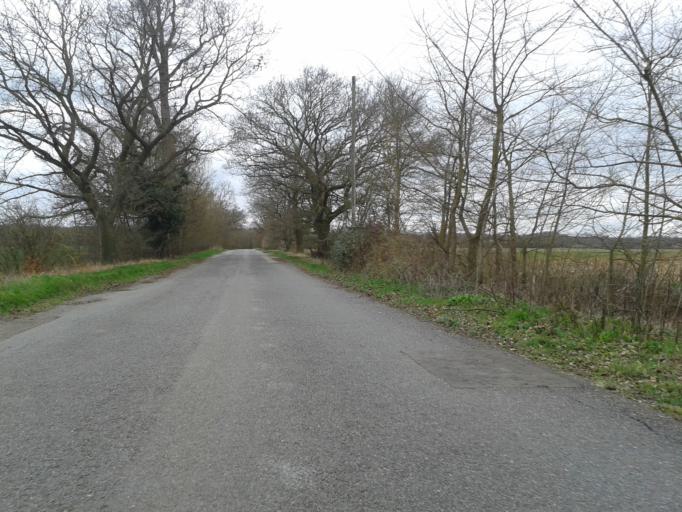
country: GB
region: England
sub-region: Cambridgeshire
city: Girton
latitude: 52.2335
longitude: 0.0518
